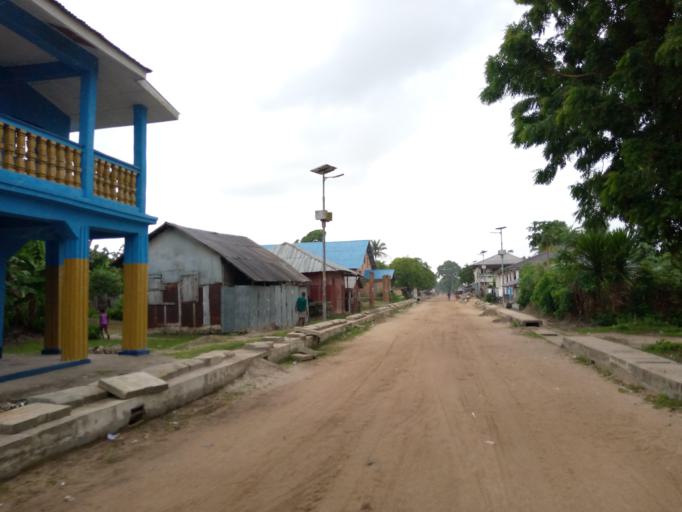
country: SL
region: Southern Province
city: Bonthe
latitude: 7.5304
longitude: -12.5032
